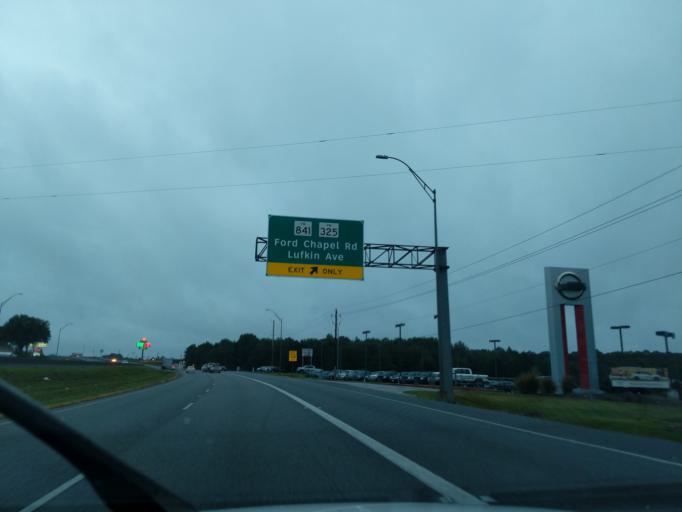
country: US
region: Texas
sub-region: Angelina County
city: Lufkin
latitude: 31.3249
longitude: -94.6932
